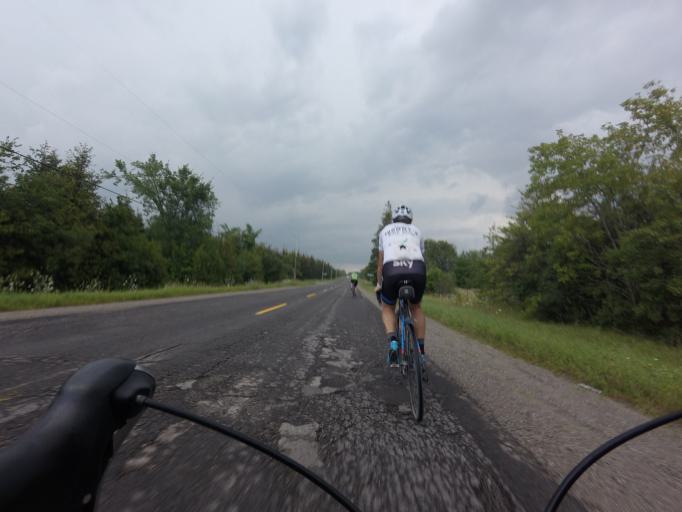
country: CA
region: Ontario
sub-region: Lanark County
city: Smiths Falls
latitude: 44.8802
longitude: -75.8156
